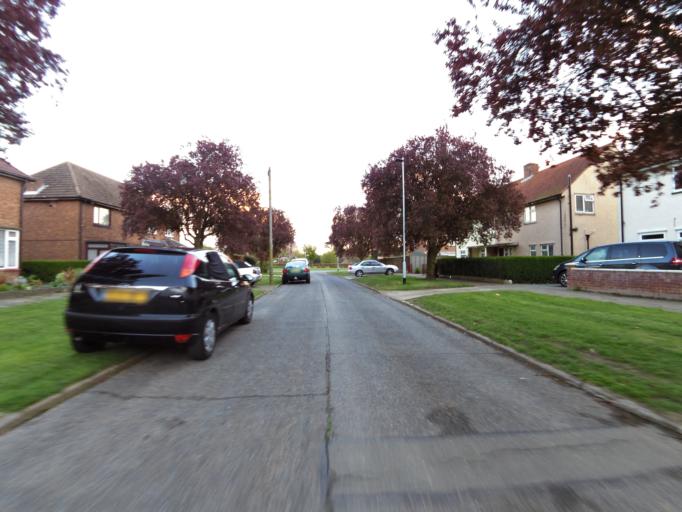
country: GB
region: England
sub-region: Suffolk
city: Kesgrave
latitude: 52.0693
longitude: 1.1959
